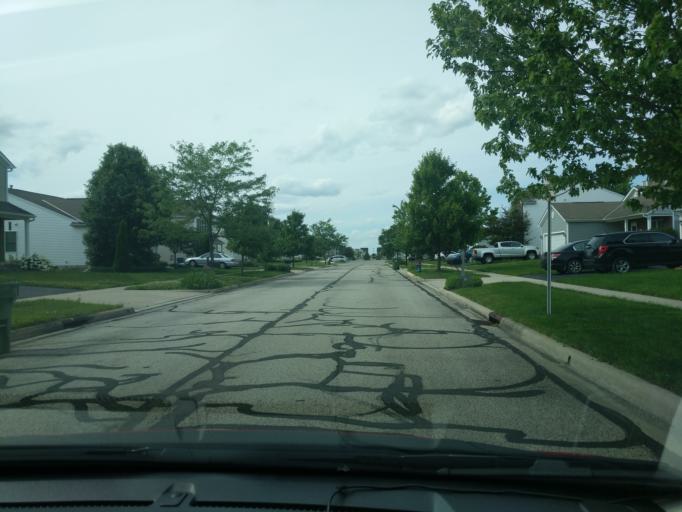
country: US
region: Ohio
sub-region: Union County
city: Marysville
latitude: 40.2679
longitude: -83.3782
